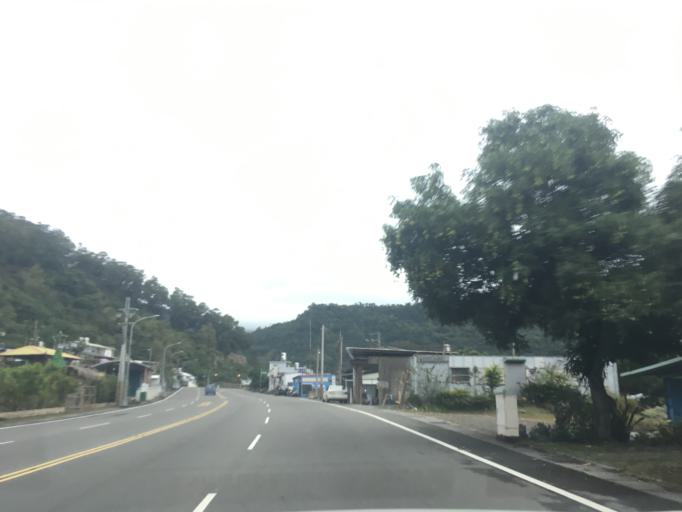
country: TW
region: Taiwan
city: Taitung City
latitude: 22.7582
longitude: 121.0514
